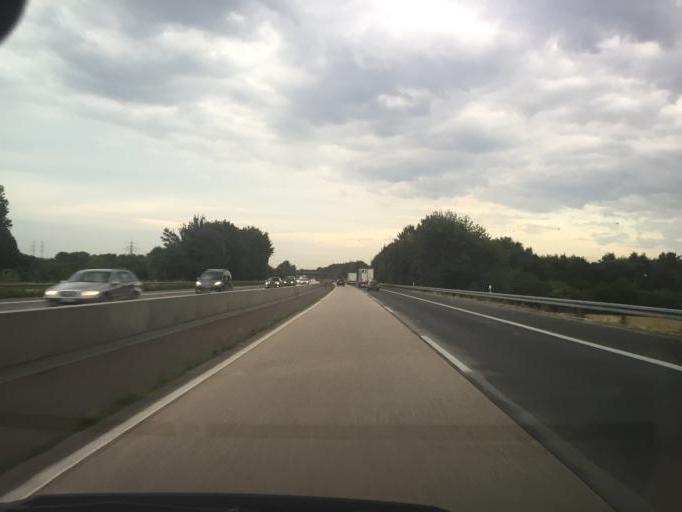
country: DE
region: North Rhine-Westphalia
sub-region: Regierungsbezirk Koln
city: Elsdorf
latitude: 50.9548
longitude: 6.5832
